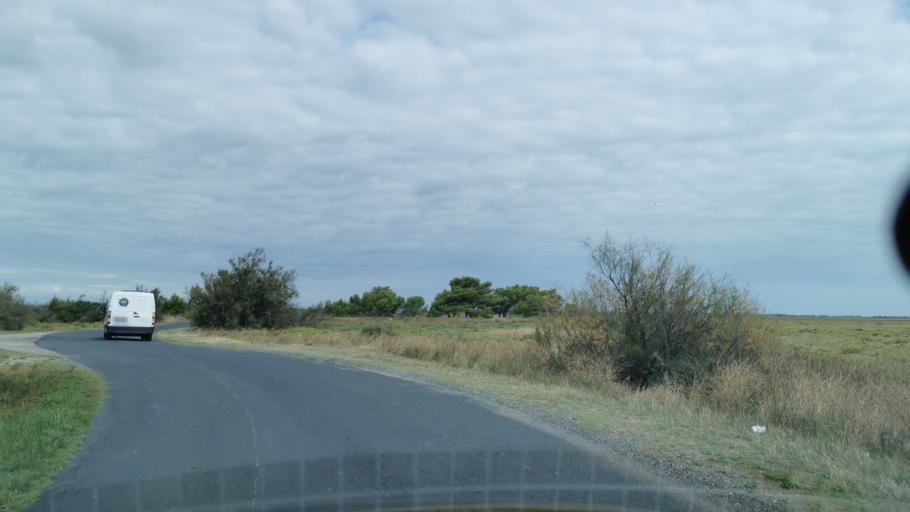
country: FR
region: Languedoc-Roussillon
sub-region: Departement de l'Aude
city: Fleury
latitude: 43.1915
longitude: 3.1968
